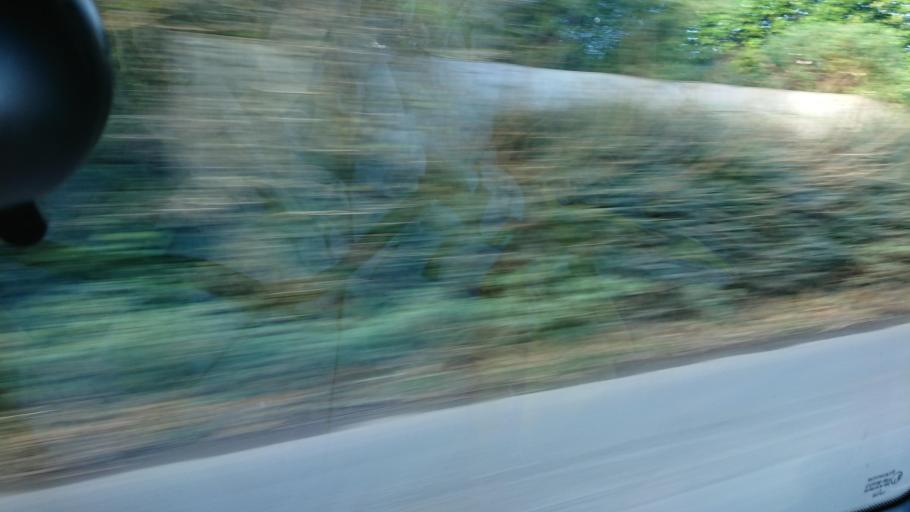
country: GB
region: England
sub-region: Devon
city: Ivybridge
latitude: 50.3606
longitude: -3.9156
